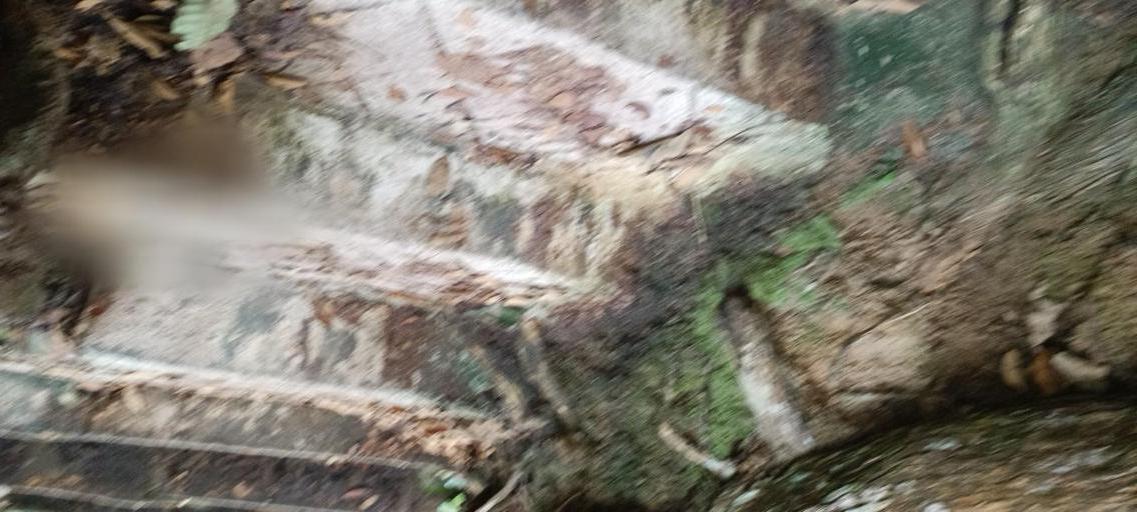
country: MY
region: Penang
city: Tanjung Tokong
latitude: 5.4334
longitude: 100.2927
